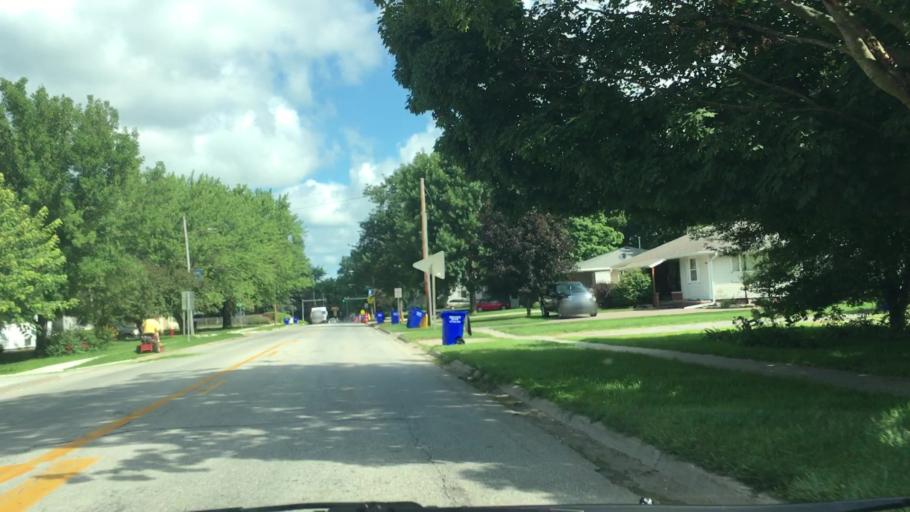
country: US
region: Iowa
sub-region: Johnson County
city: Solon
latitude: 41.8032
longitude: -91.4920
